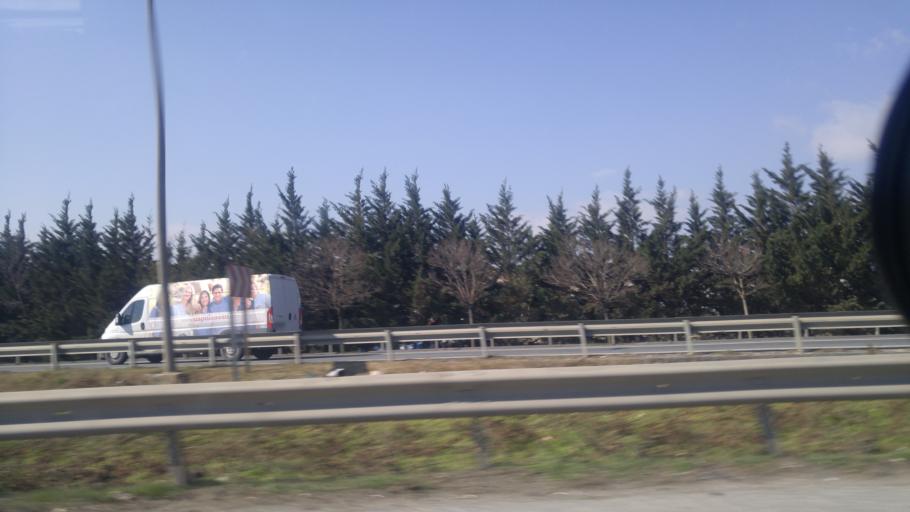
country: TR
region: Istanbul
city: Muratbey
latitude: 41.0913
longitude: 28.5098
